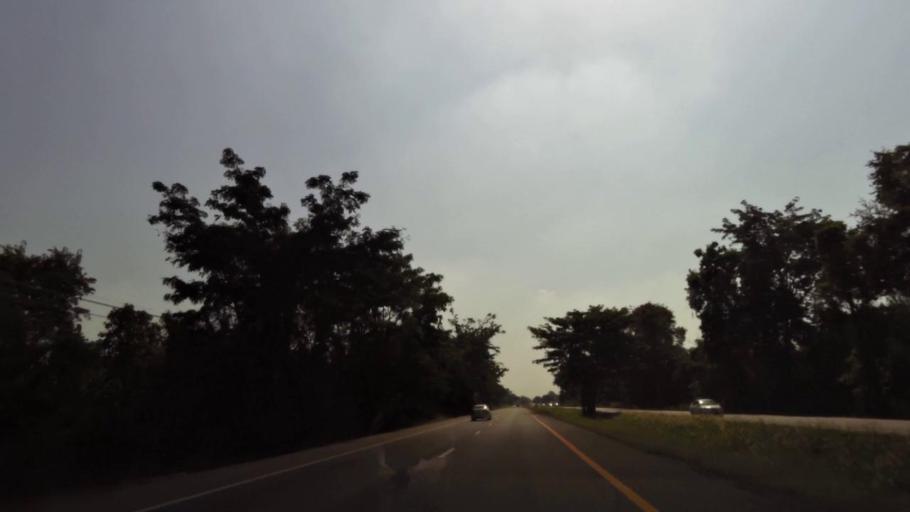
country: TH
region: Phichit
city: Bueng Na Rang
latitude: 16.2003
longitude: 100.1280
